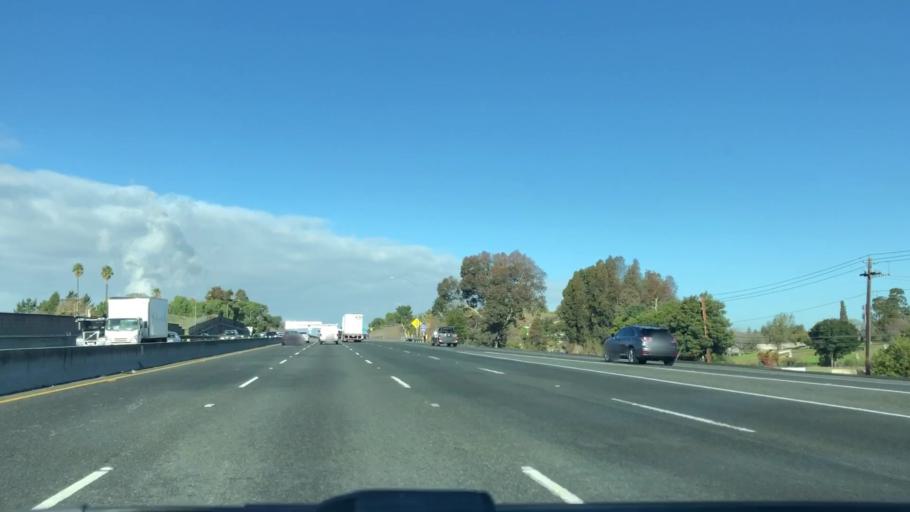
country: US
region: California
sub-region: Contra Costa County
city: Pacheco
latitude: 37.9971
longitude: -122.0729
